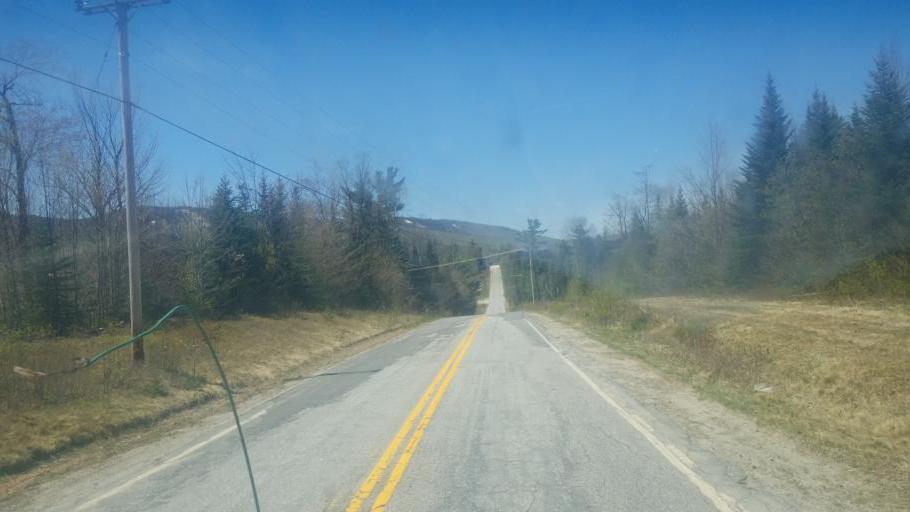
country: US
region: New Hampshire
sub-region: Coos County
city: Jefferson
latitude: 44.2608
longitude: -71.4342
